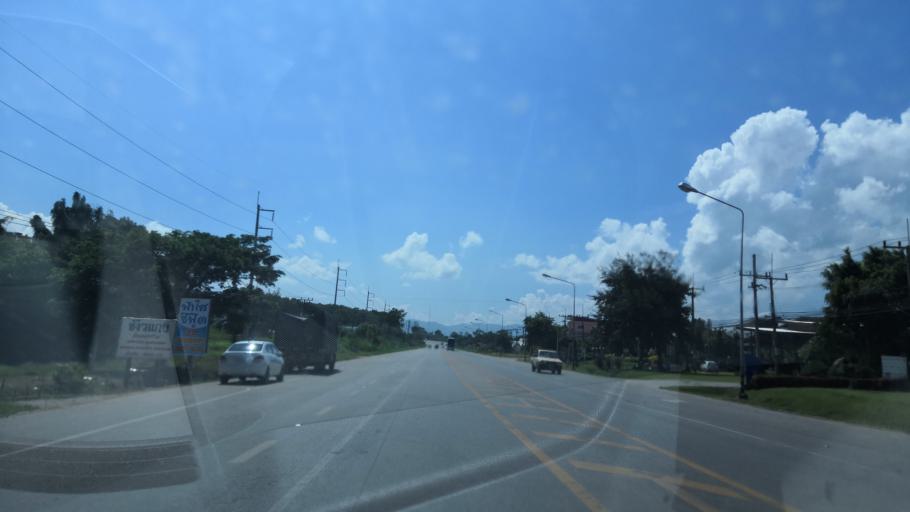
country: TH
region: Chiang Rai
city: Mae Suai
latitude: 19.6473
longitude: 99.5325
